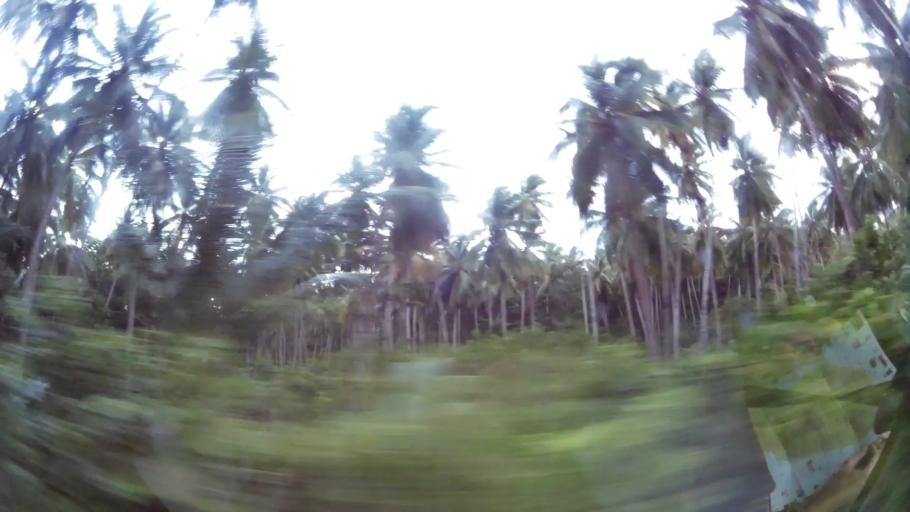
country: DM
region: Saint Andrew
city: Calibishie
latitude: 15.5943
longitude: -61.3633
